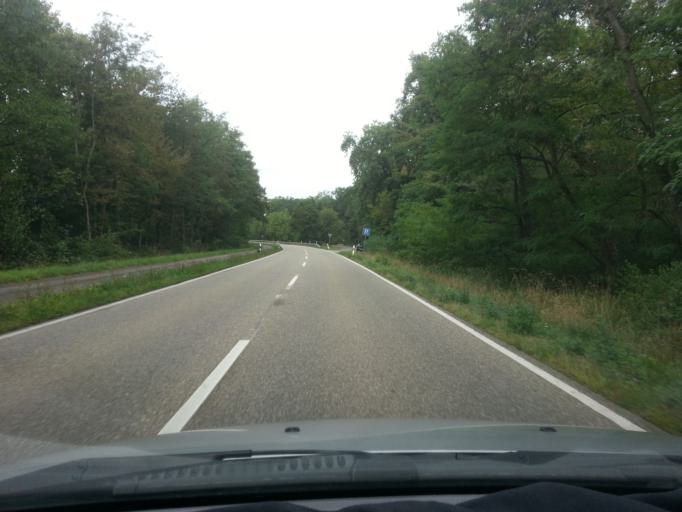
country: DE
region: Rheinland-Pfalz
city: Offenbach an der Queich
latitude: 49.2097
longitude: 8.1897
